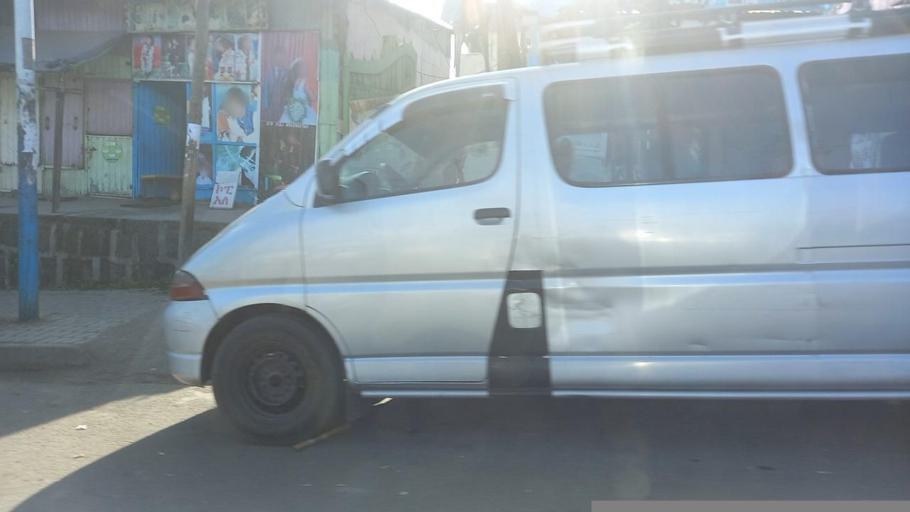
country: ET
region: Adis Abeba
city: Addis Ababa
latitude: 8.9343
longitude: 38.7440
